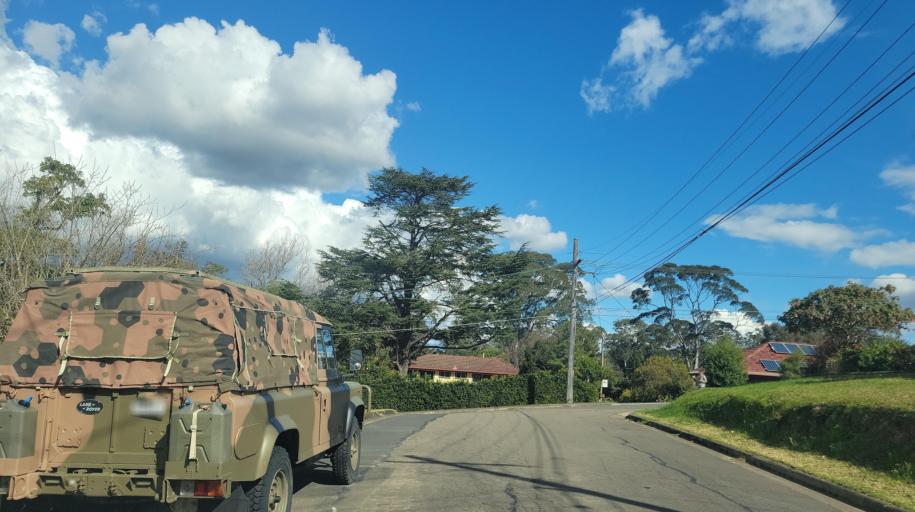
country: AU
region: New South Wales
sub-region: Hornsby Shire
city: Pennant Hills
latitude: -33.7367
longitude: 151.0777
